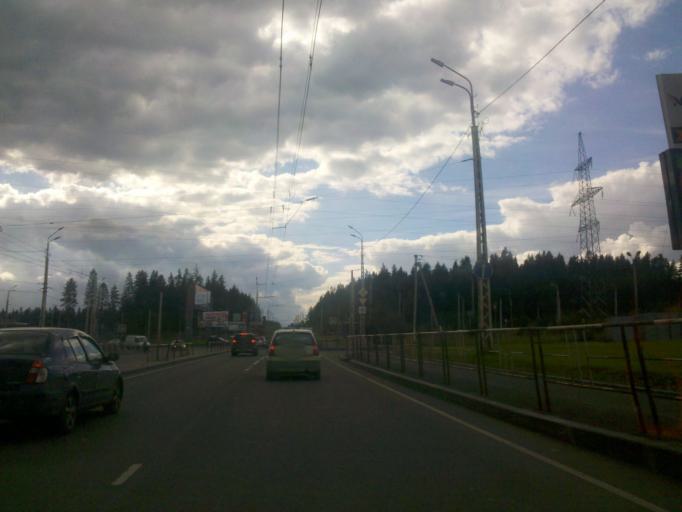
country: RU
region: Republic of Karelia
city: Petrozavodsk
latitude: 61.7794
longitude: 34.3106
